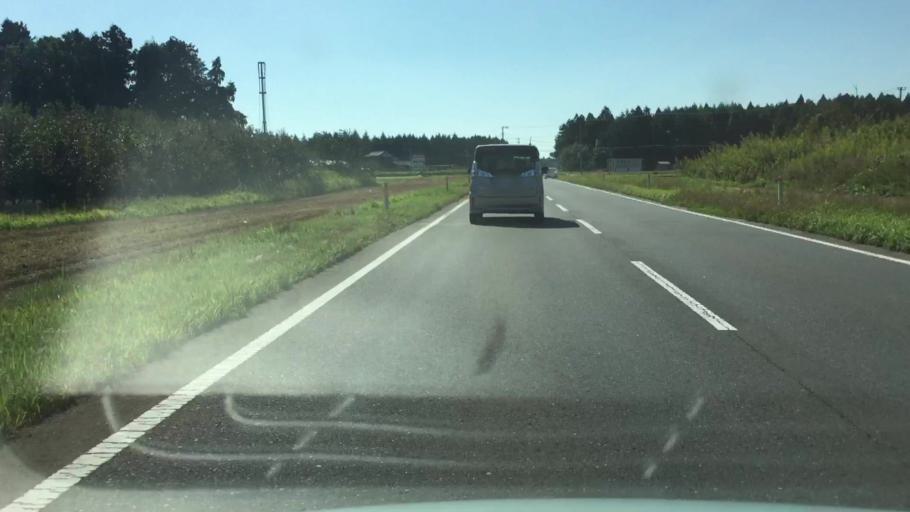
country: JP
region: Ibaraki
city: Ami
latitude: 35.9860
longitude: 140.1854
